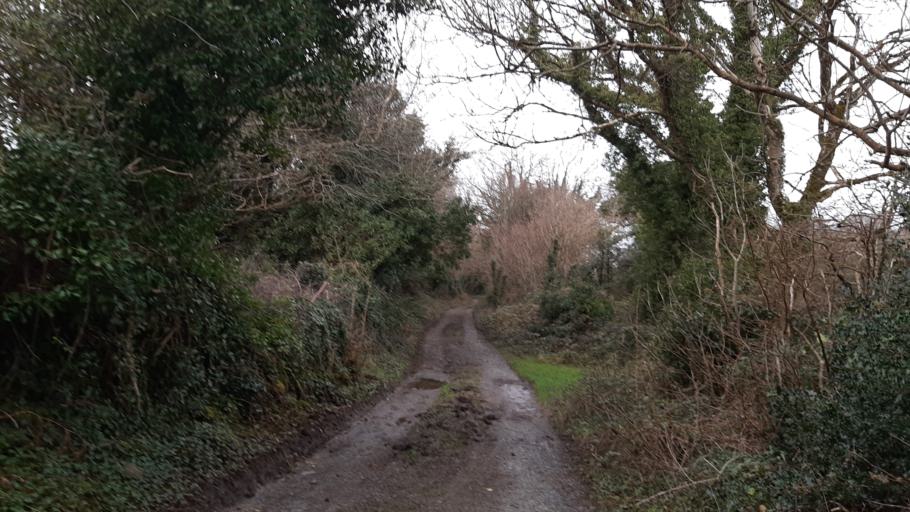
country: IE
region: Connaught
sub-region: County Galway
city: Gaillimh
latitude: 53.2968
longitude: -9.0676
